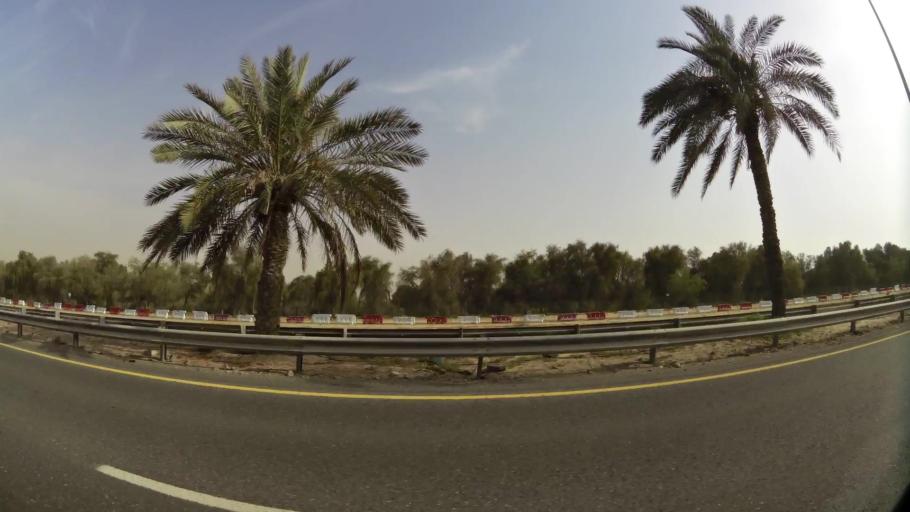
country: AE
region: Ash Shariqah
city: Sharjah
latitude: 25.2317
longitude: 55.4455
